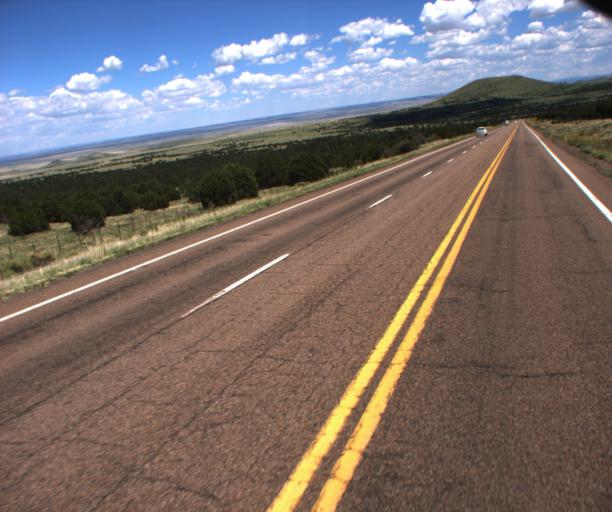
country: US
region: Arizona
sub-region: Apache County
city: Springerville
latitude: 34.2650
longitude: -109.5711
